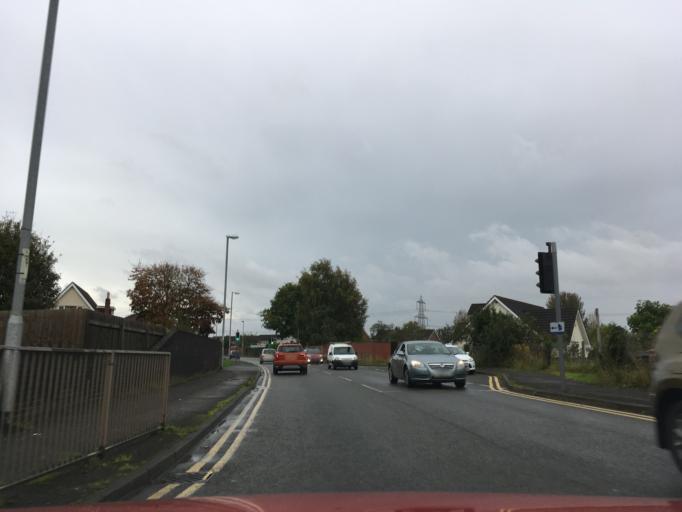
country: GB
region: Wales
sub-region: Monmouthshire
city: Caldicot
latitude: 51.5873
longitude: -2.7583
